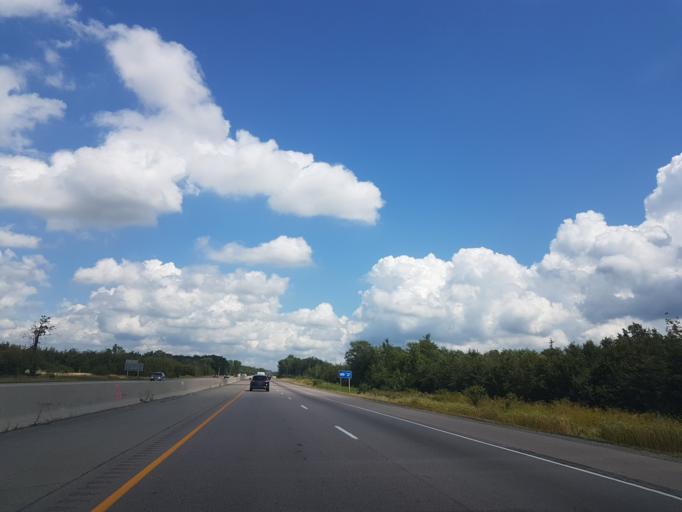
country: CA
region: Ontario
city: Belleville
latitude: 44.2010
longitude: -77.3706
